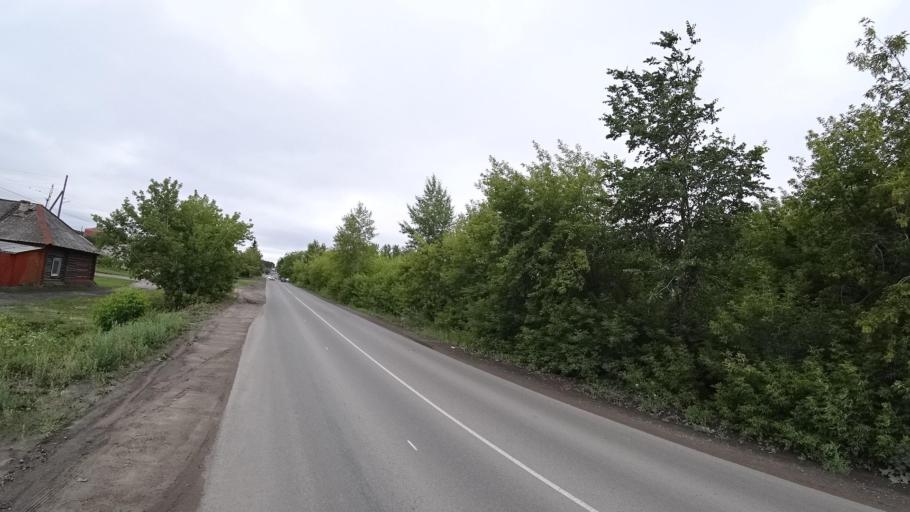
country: RU
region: Sverdlovsk
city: Kamyshlov
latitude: 56.8411
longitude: 62.7350
